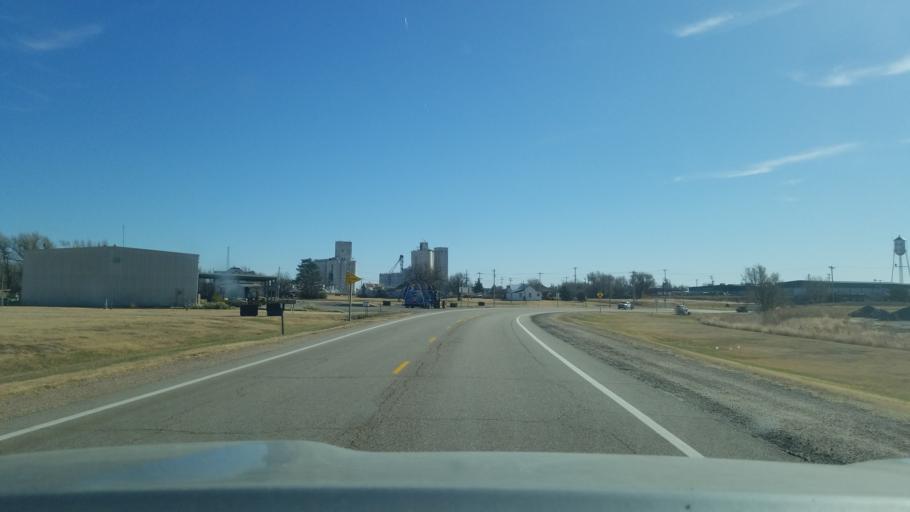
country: US
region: Kansas
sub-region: Kiowa County
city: Greensburg
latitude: 37.5539
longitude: -99.6386
